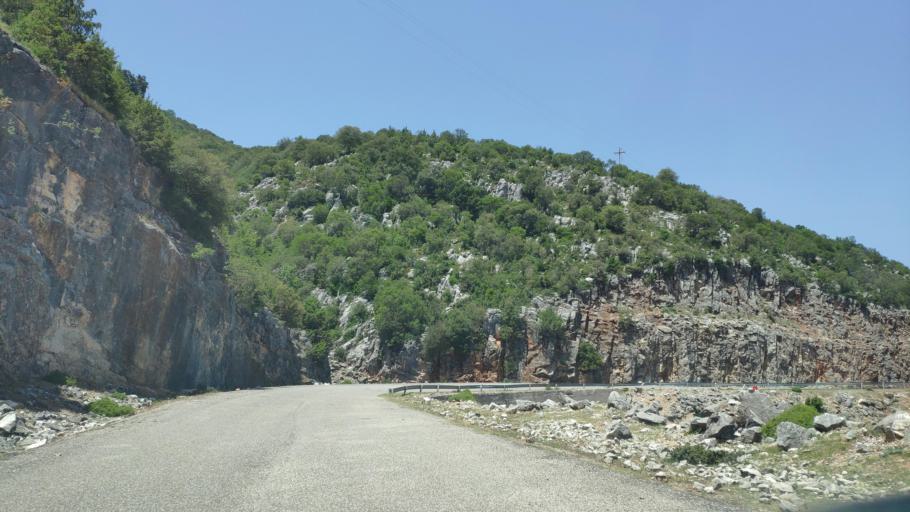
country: GR
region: Thessaly
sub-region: Nomos Kardhitsas
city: Anthiro
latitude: 39.1237
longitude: 21.3993
